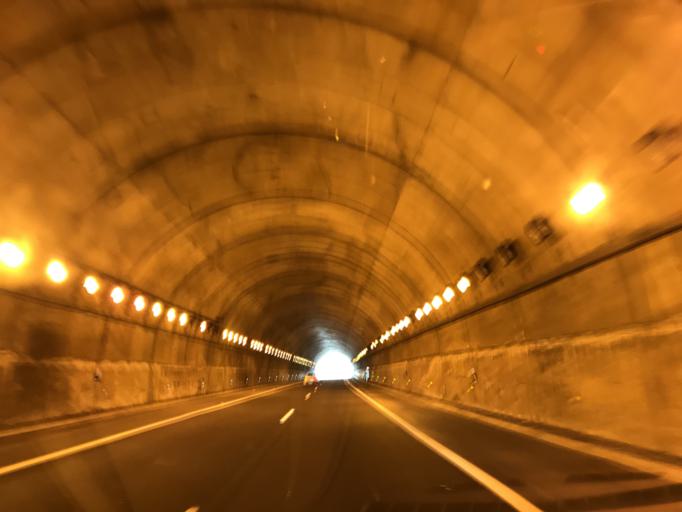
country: ES
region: Andalusia
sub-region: Provincia de Malaga
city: Istan
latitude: 36.5259
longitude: -4.9607
